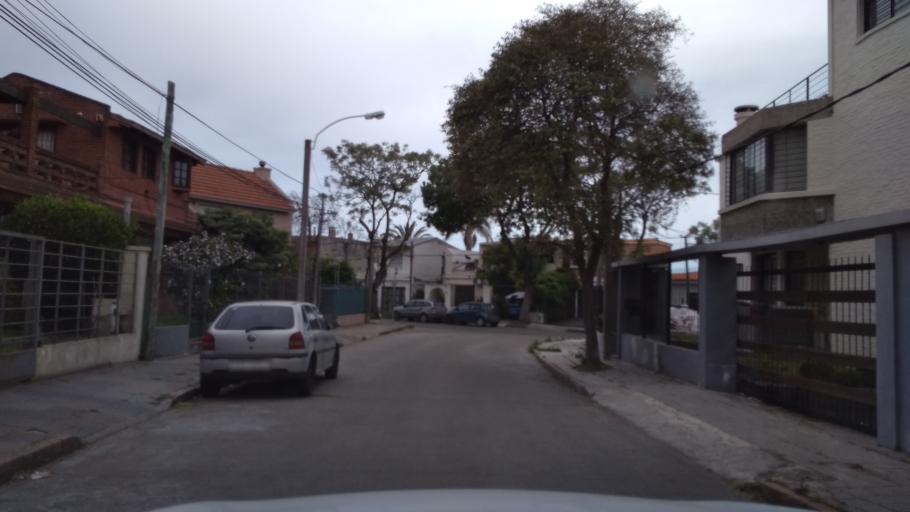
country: UY
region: Montevideo
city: Montevideo
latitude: -34.9040
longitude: -56.1277
